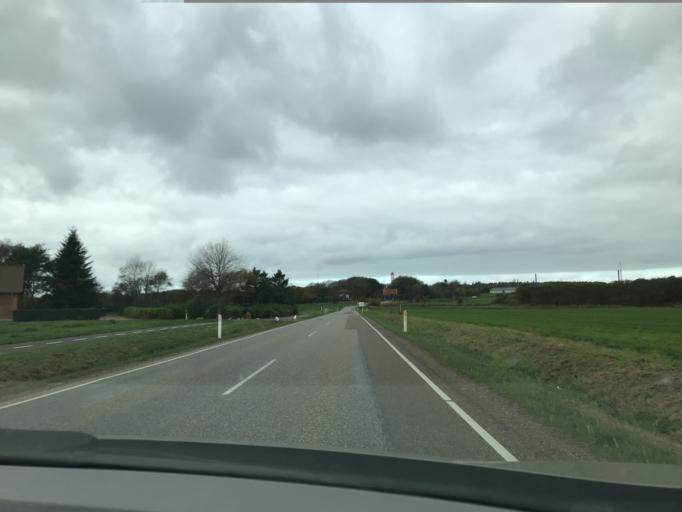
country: DK
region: South Denmark
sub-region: Varde Kommune
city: Olgod
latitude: 55.8018
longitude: 8.6355
